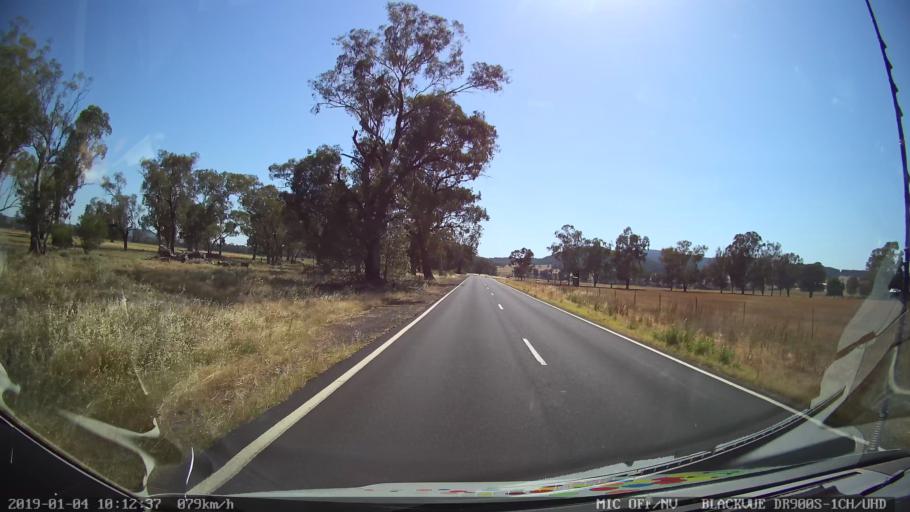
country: AU
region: New South Wales
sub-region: Cabonne
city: Canowindra
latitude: -33.4120
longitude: 148.3970
